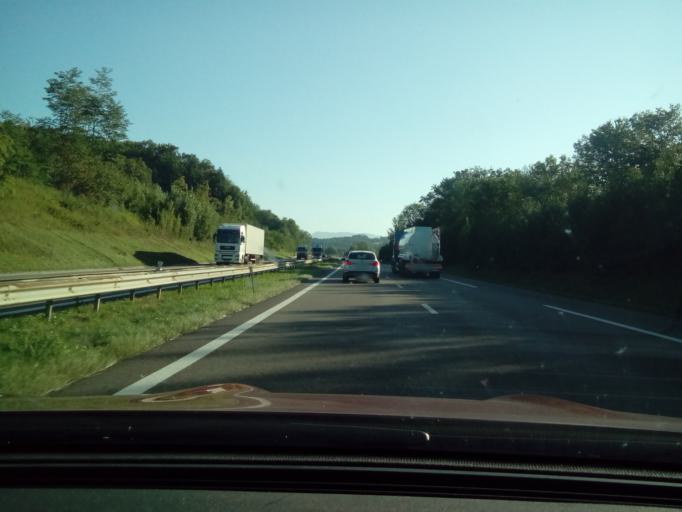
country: FR
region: Rhone-Alpes
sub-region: Departement de la Haute-Savoie
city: Alby-sur-Cheran
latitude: 45.8293
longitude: 6.0405
